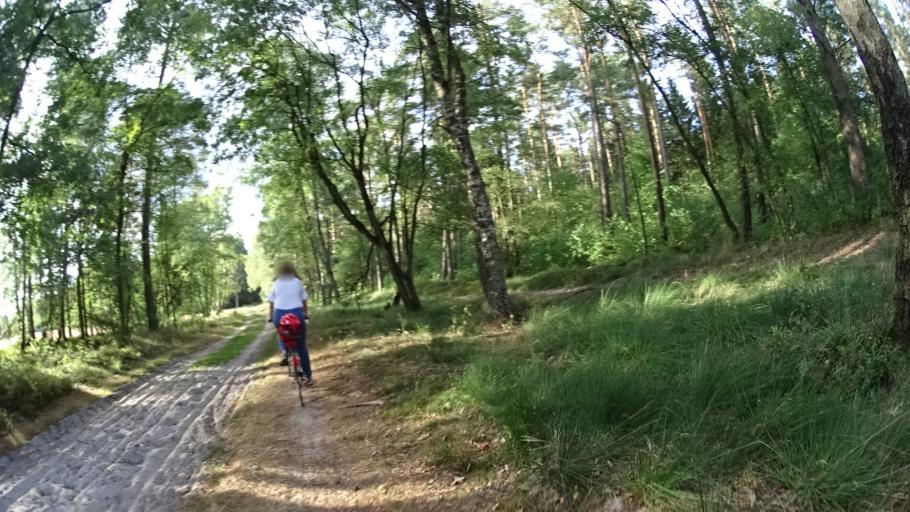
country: DE
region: Lower Saxony
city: Handeloh
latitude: 53.2227
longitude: 9.8769
